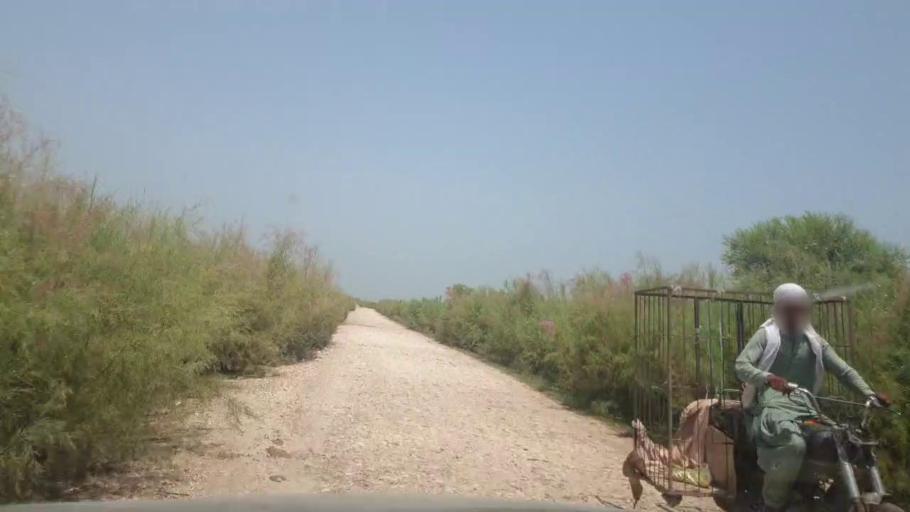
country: PK
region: Sindh
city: Lakhi
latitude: 27.8418
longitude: 68.6269
